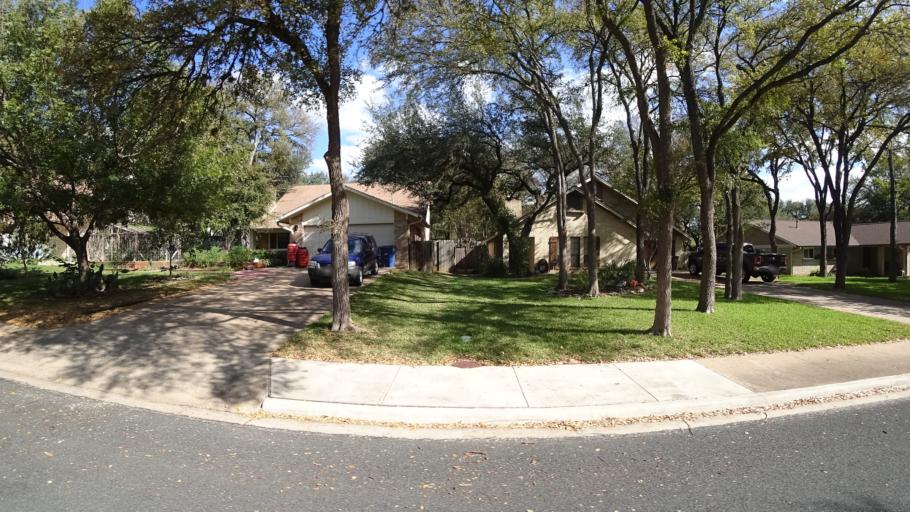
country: US
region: Texas
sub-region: Williamson County
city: Jollyville
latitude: 30.4155
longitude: -97.7271
